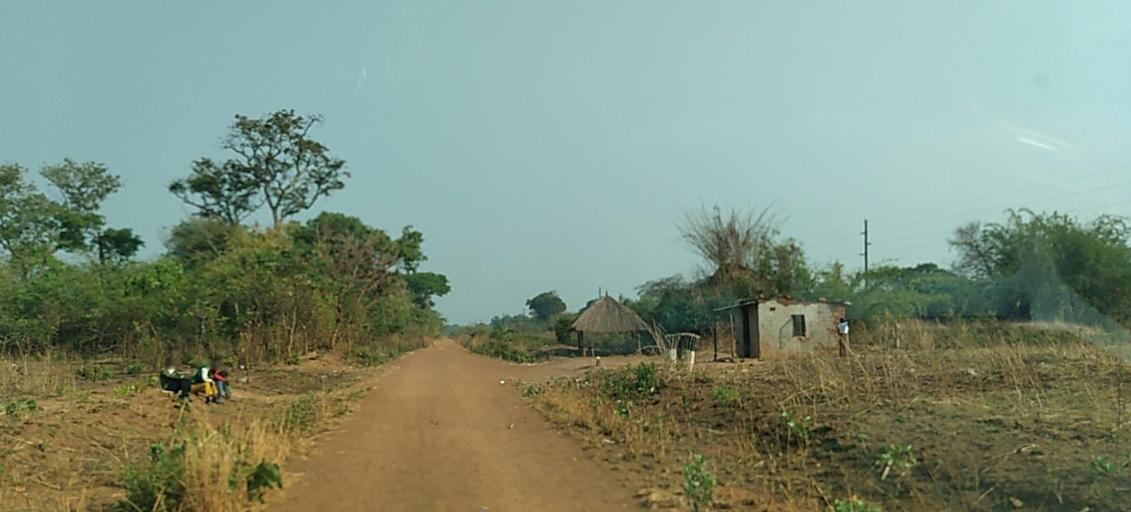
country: ZM
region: Copperbelt
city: Chingola
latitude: -12.8504
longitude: 27.5513
